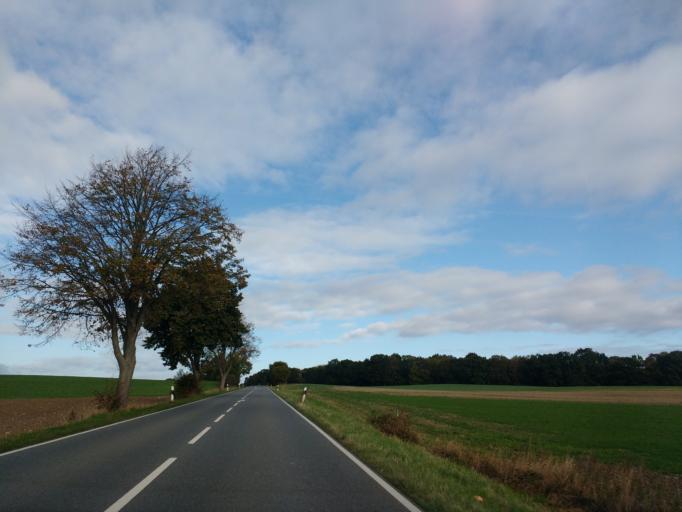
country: DE
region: Schleswig-Holstein
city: Altenkrempe
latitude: 54.1466
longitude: 10.8206
